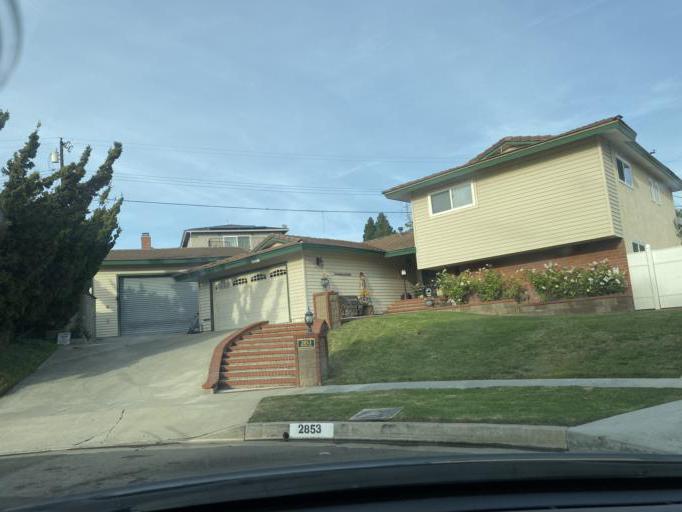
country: US
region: California
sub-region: Orange County
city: Placentia
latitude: 33.8985
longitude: -117.8781
